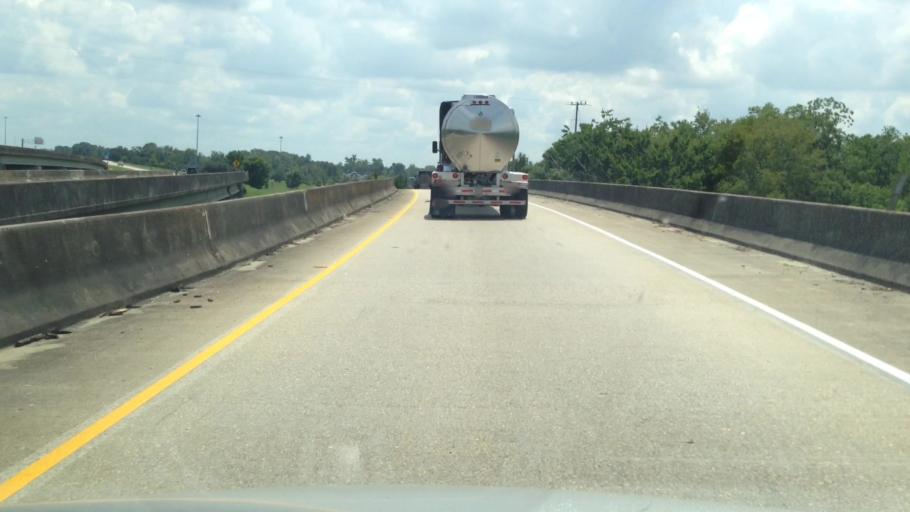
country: US
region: Louisiana
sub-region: Saint Landry Parish
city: Opelousas
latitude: 30.5374
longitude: -92.0638
